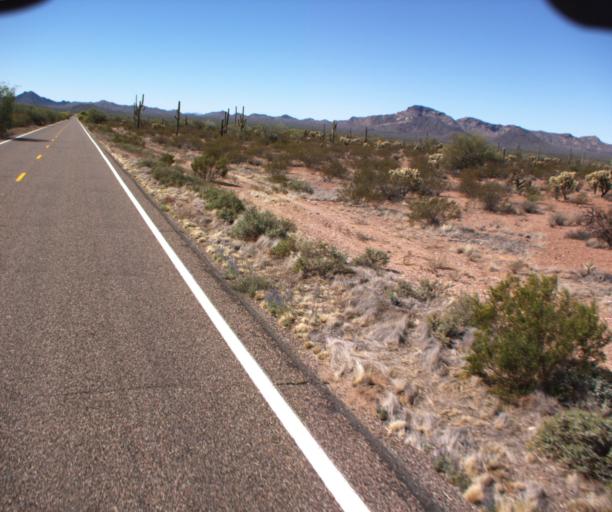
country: MX
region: Sonora
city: Sonoyta
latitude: 32.0534
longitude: -112.7901
